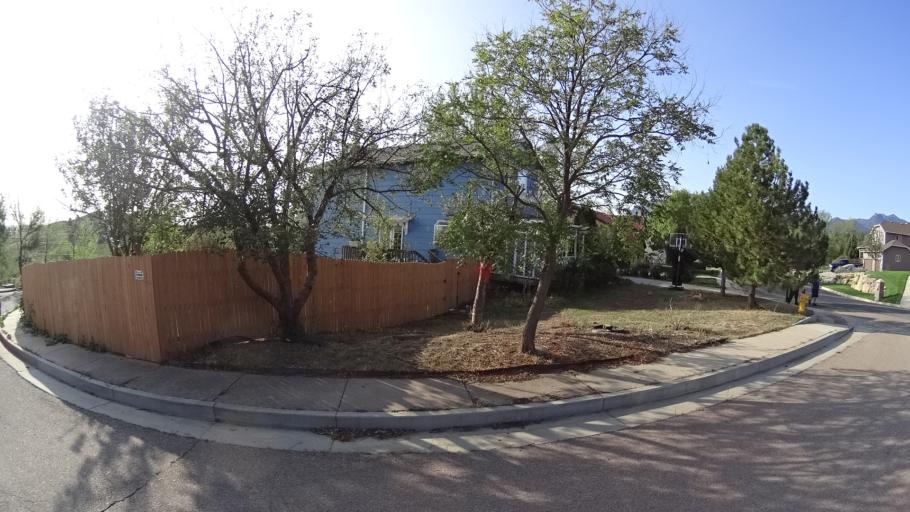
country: US
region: Colorado
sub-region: El Paso County
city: Colorado Springs
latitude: 38.8170
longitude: -104.8511
